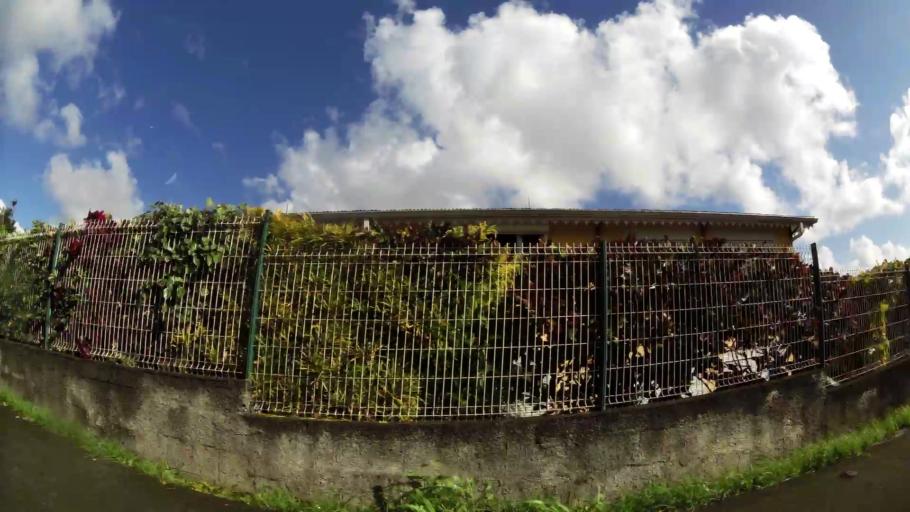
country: MQ
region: Martinique
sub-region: Martinique
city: Fort-de-France
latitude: 14.6339
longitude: -61.0732
